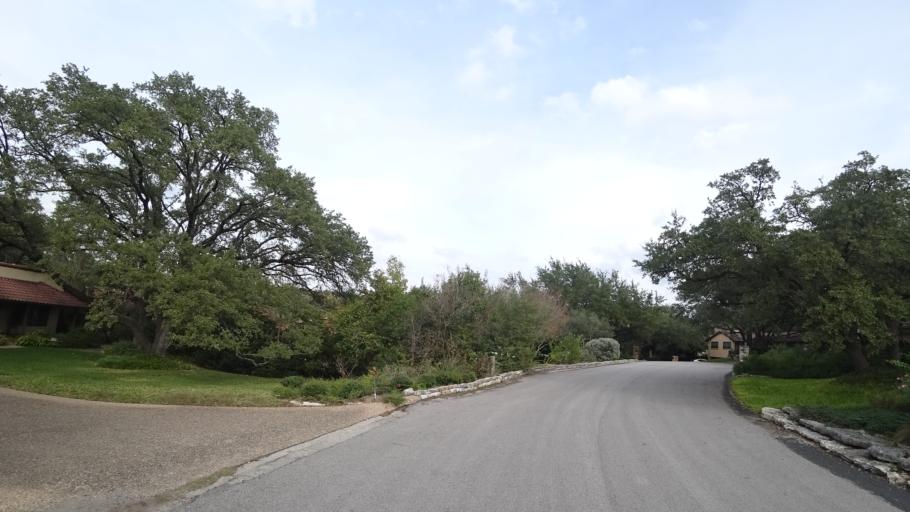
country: US
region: Texas
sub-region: Travis County
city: Hudson Bend
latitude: 30.3908
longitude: -97.8920
